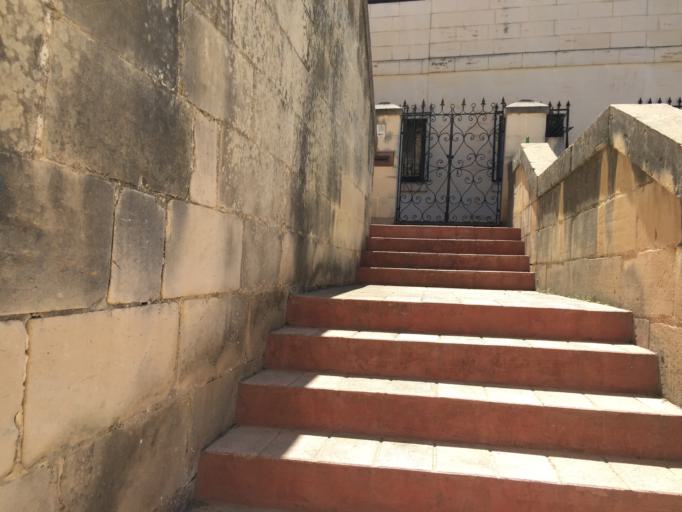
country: MT
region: Saint Julian
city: San Giljan
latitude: 35.9142
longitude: 14.4845
